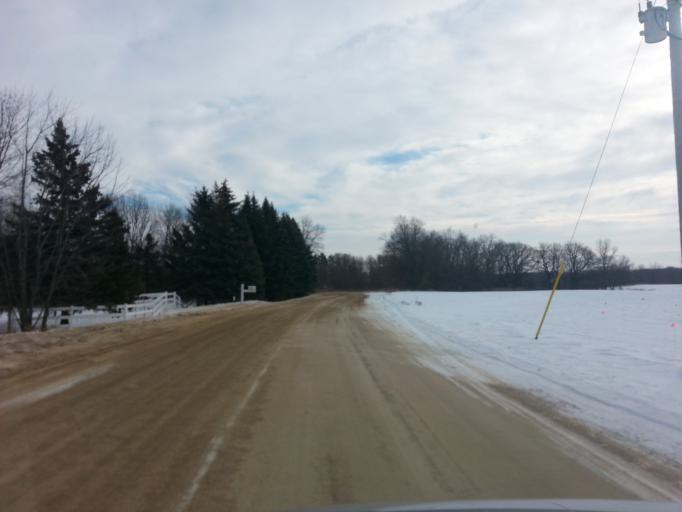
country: US
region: Minnesota
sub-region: Scott County
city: Prior Lake
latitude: 44.7199
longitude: -93.4762
